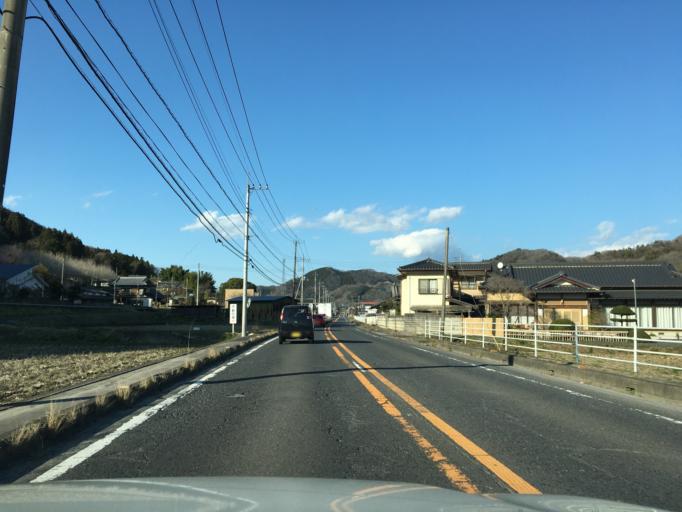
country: JP
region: Ibaraki
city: Omiya
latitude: 36.6409
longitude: 140.3915
